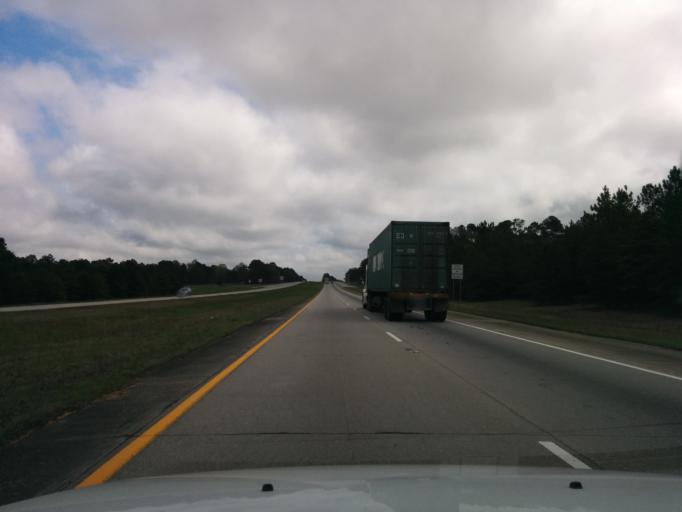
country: US
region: Georgia
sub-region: Emanuel County
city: Swainsboro
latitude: 32.4180
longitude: -82.3919
